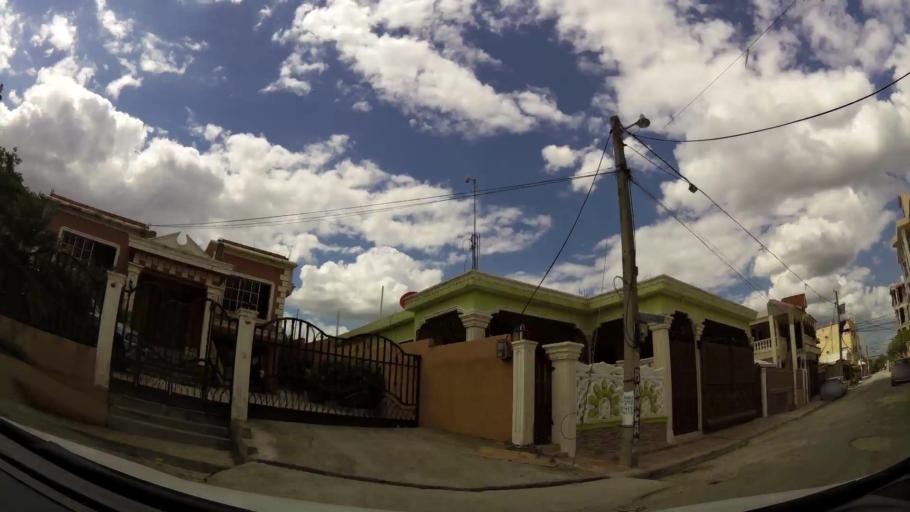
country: DO
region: Nacional
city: Ensanche Luperon
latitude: 18.5258
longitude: -69.8952
